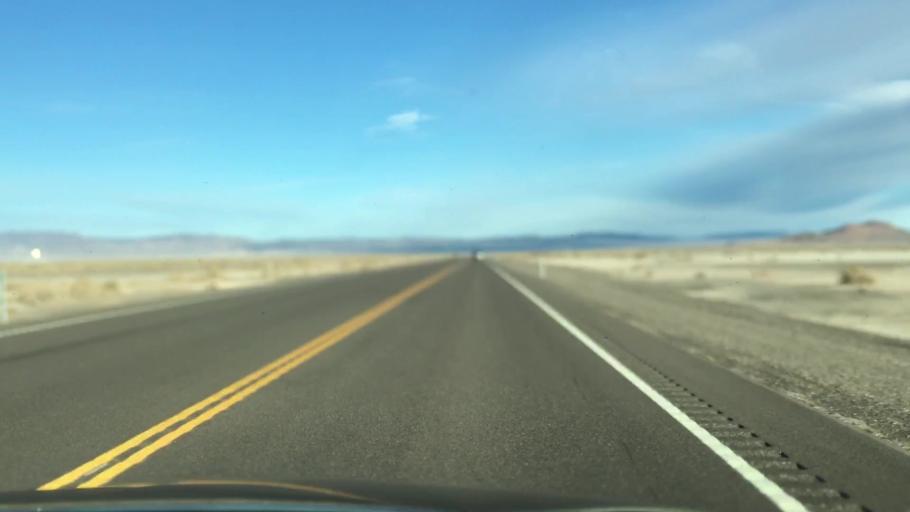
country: US
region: Nevada
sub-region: Nye County
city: Tonopah
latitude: 38.1293
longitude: -117.5600
